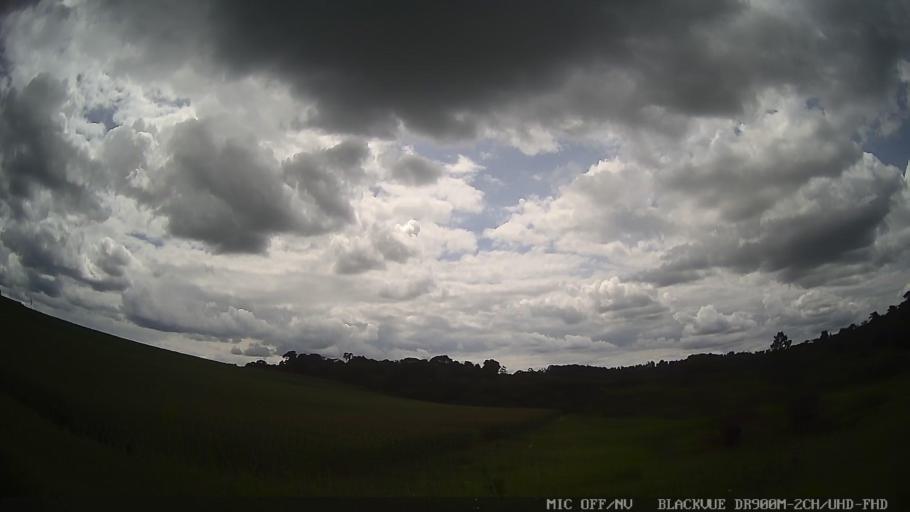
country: BR
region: Sao Paulo
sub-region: Rio Grande Da Serra
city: Rio Grande da Serra
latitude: -23.6906
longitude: -46.2632
